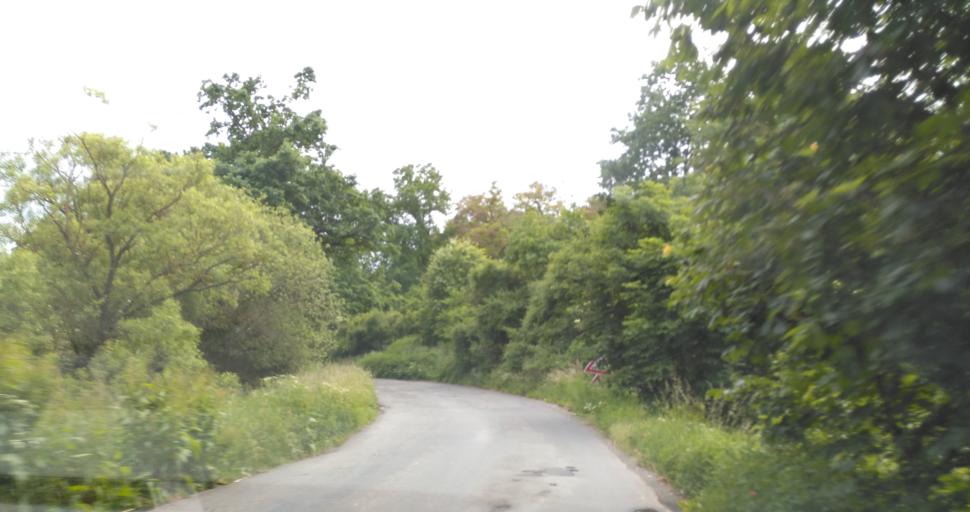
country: CZ
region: Central Bohemia
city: Hostomice
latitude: 49.8647
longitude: 14.0423
